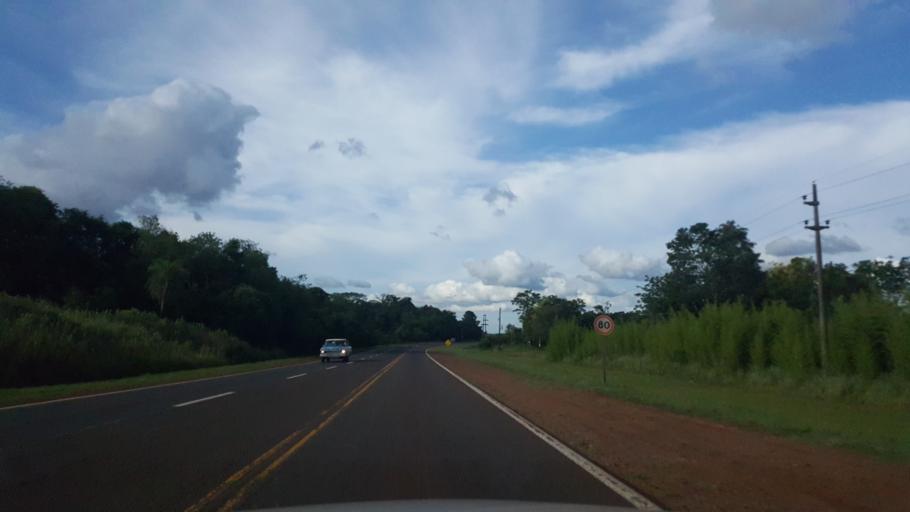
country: AR
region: Misiones
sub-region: Departamento de Candelaria
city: Loreto
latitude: -27.3345
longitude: -55.5439
